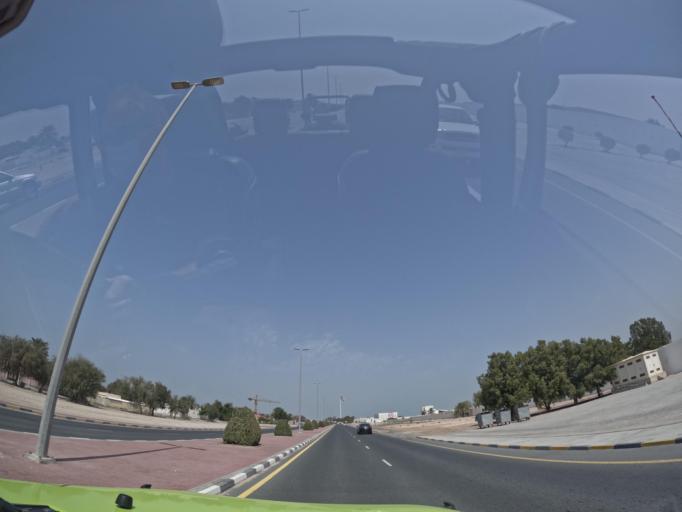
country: AE
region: Umm al Qaywayn
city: Umm al Qaywayn
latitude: 25.5572
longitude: 55.5619
